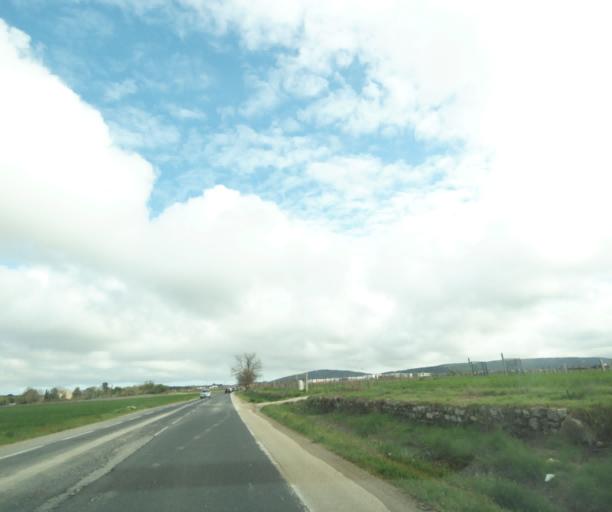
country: FR
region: Languedoc-Roussillon
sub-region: Departement de l'Herault
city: Saussan
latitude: 43.5671
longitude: 3.7869
